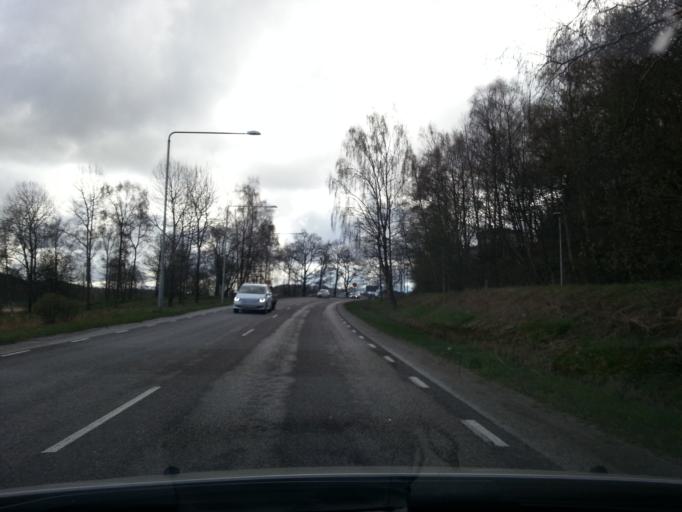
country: SE
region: Vaestra Goetaland
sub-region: Goteborg
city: Goeteborg
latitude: 57.7580
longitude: 11.9397
